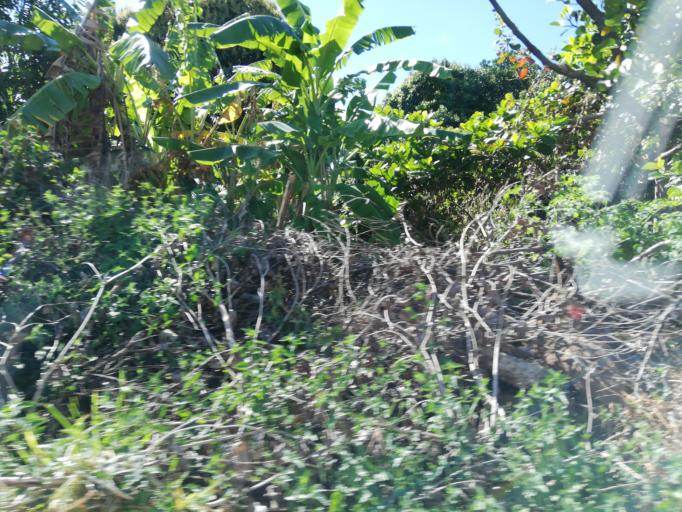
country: MU
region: Moka
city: Moka
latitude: -20.2205
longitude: 57.4668
